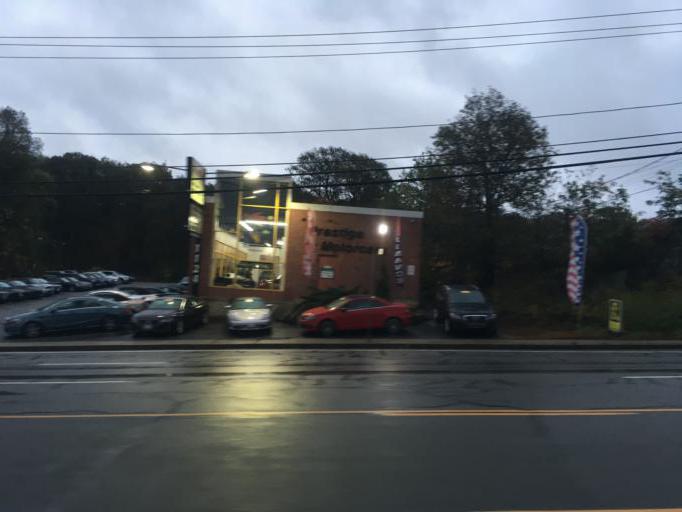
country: US
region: Rhode Island
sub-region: Kent County
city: West Warwick
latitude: 41.7084
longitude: -71.4914
